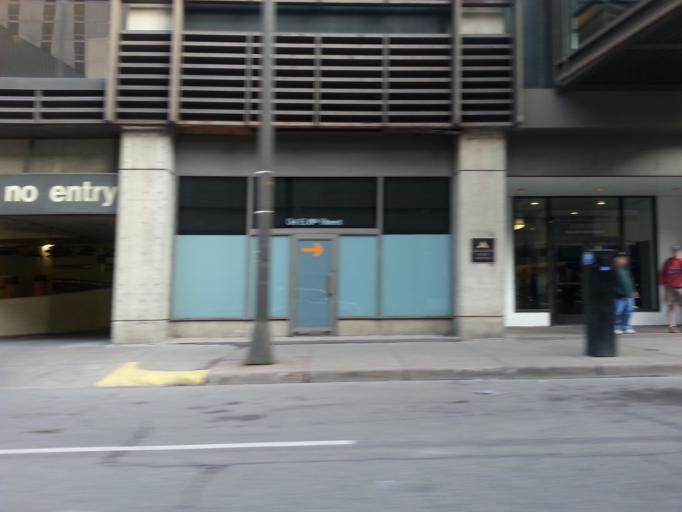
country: US
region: Minnesota
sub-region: Ramsey County
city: Saint Paul
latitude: 44.9473
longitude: -93.0935
